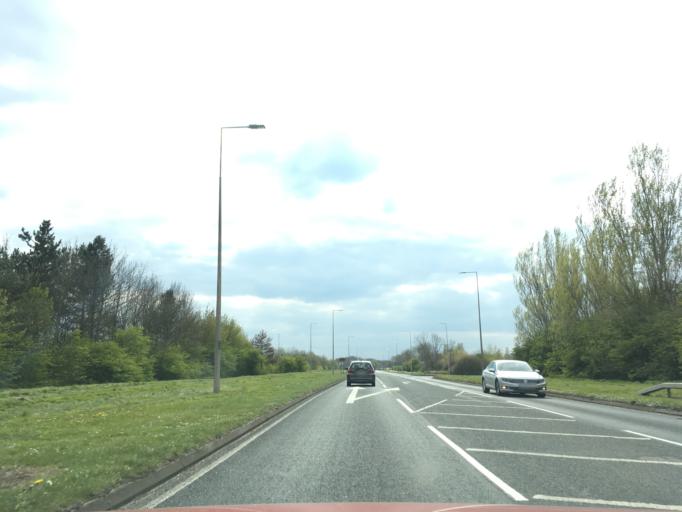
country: GB
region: England
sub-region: Milton Keynes
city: Shenley Church End
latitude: 52.0074
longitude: -0.7848
